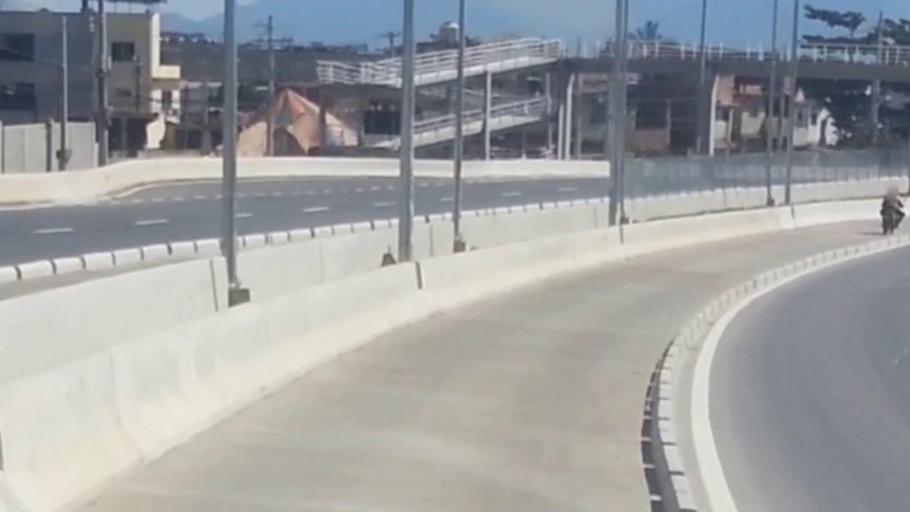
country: BR
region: Rio de Janeiro
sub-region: Nilopolis
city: Nilopolis
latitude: -22.8799
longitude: -43.4002
